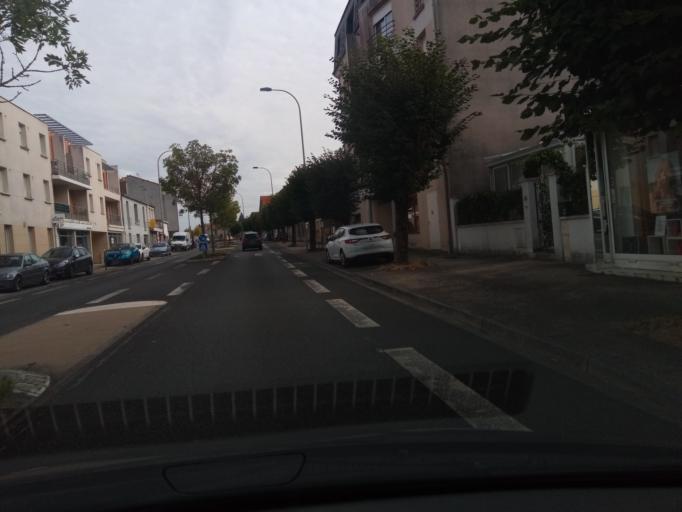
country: FR
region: Poitou-Charentes
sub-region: Departement de la Vienne
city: Biard
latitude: 46.5621
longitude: 0.3157
